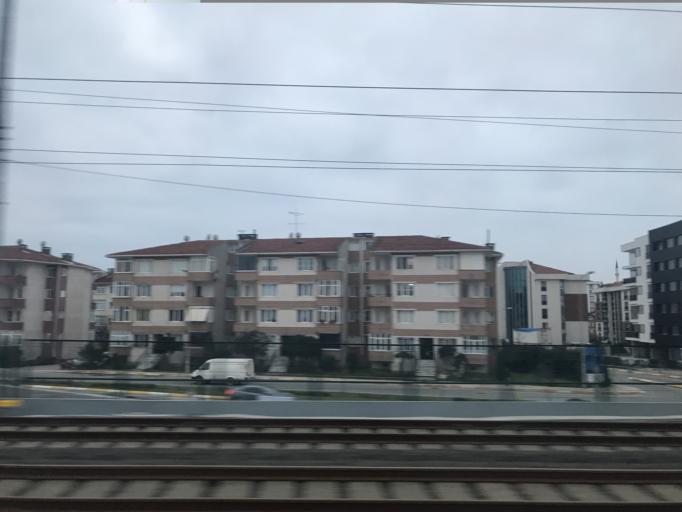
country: TR
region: Istanbul
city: Icmeler
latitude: 40.8340
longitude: 29.3159
